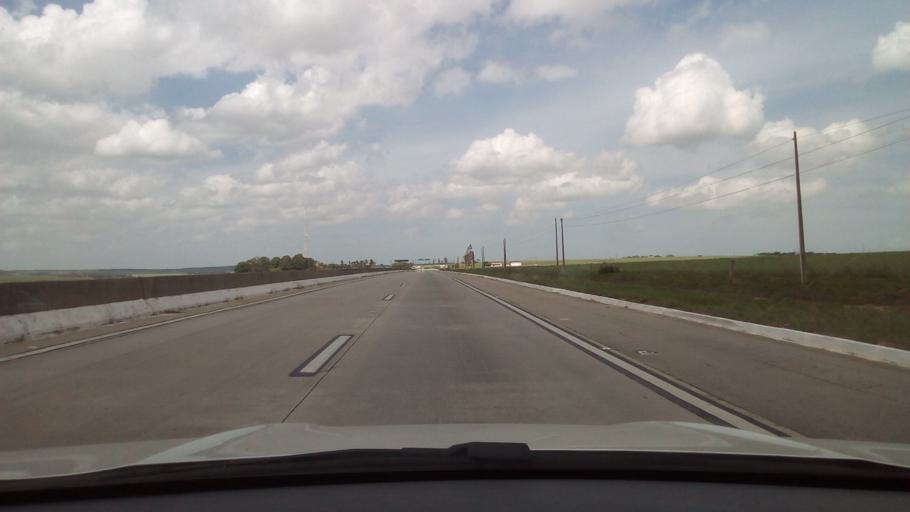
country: BR
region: Paraiba
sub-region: Mamanguape
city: Mamanguape
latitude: -6.8006
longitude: -35.1391
